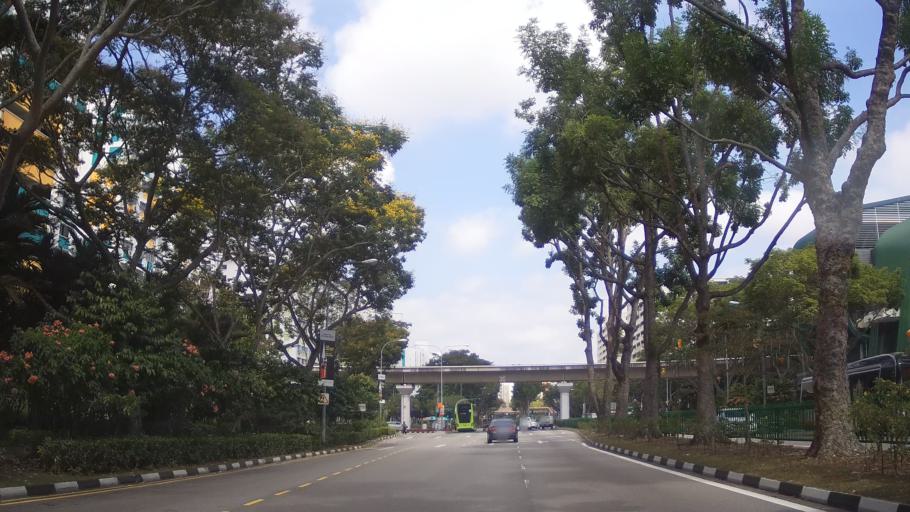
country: MY
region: Johor
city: Johor Bahru
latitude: 1.3767
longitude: 103.7730
